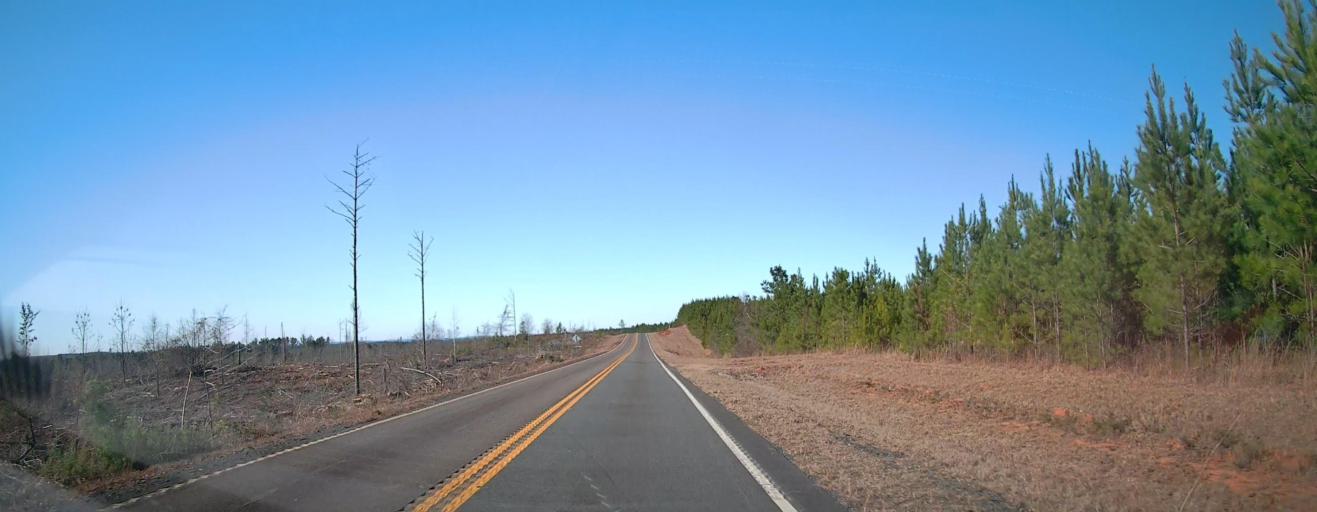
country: US
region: Georgia
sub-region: Talbot County
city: Talbotton
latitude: 32.6536
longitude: -84.4566
